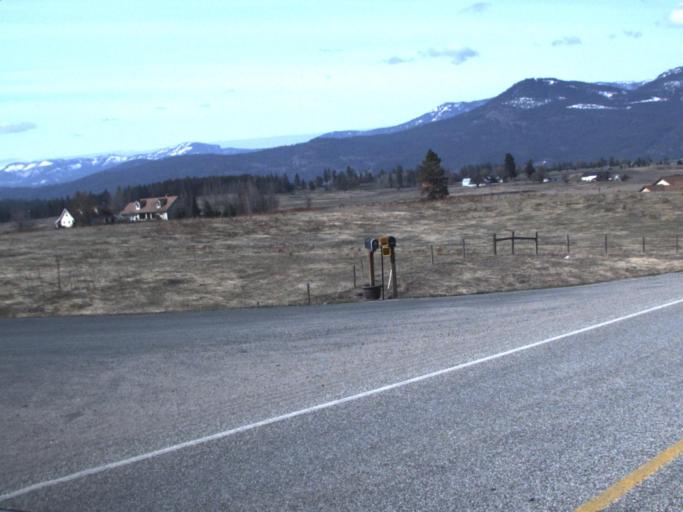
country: US
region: Washington
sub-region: Stevens County
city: Colville
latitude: 48.5475
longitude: -117.8593
